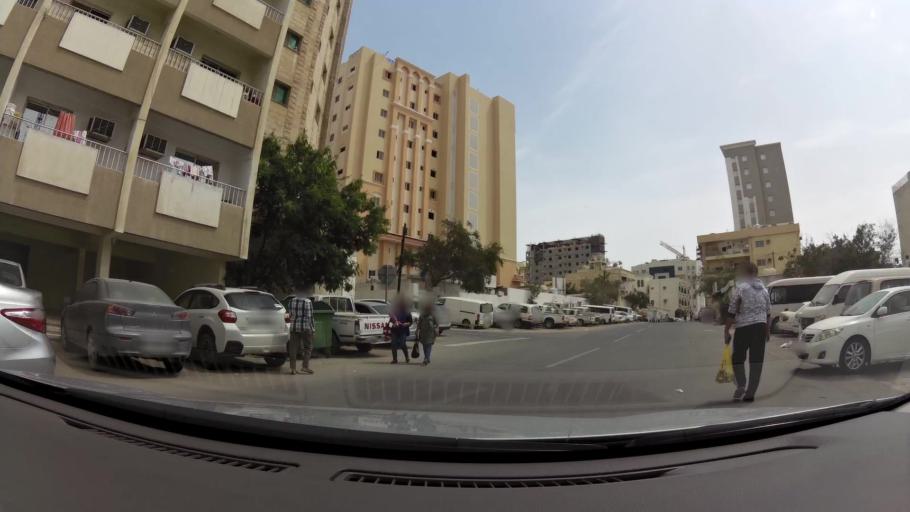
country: QA
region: Baladiyat ad Dawhah
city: Doha
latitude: 25.2789
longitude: 51.5225
